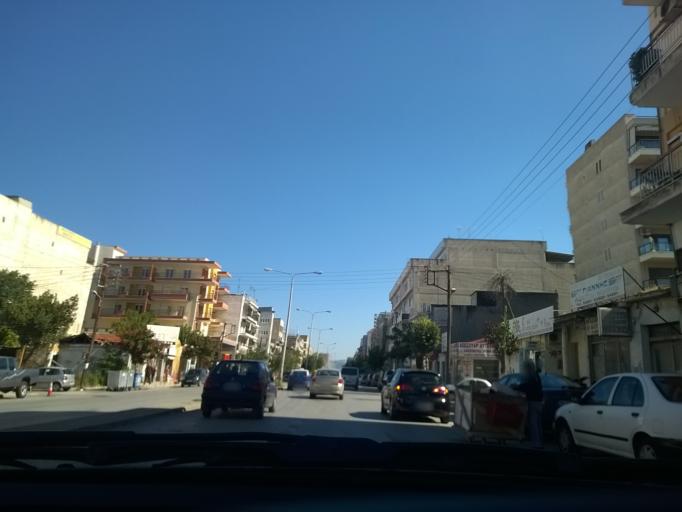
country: GR
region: Central Macedonia
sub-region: Nomos Thessalonikis
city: Ampelokipoi
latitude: 40.6512
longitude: 22.9147
